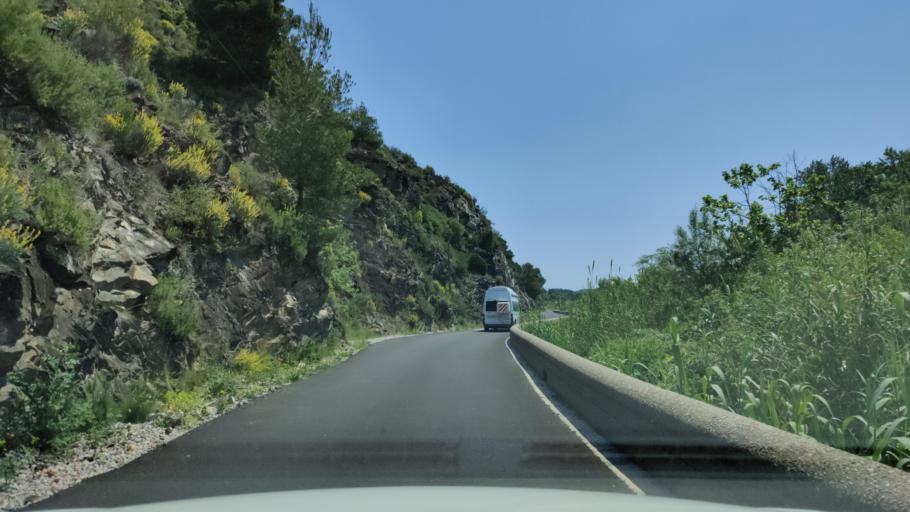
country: FR
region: Languedoc-Roussillon
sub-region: Departement des Pyrenees-Orientales
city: Baixas
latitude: 42.7853
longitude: 2.7724
